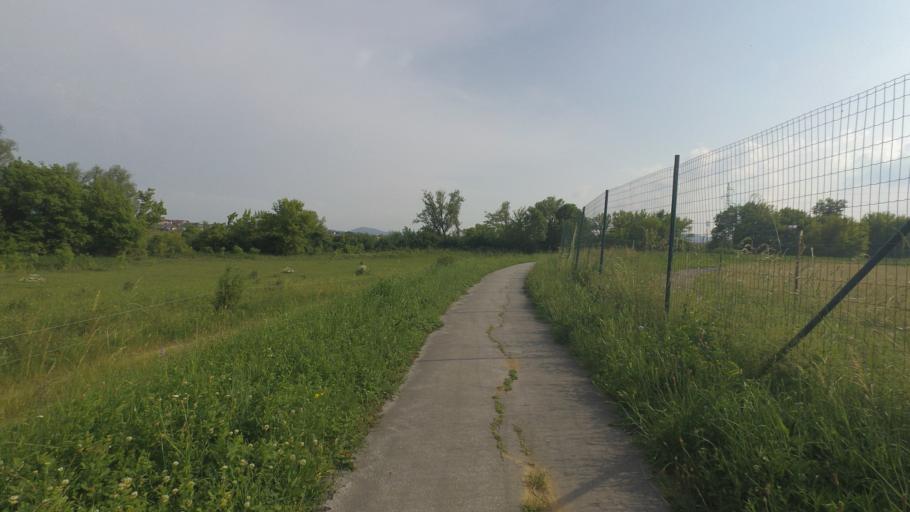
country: HR
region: Karlovacka
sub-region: Grad Karlovac
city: Karlovac
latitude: 45.4907
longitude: 15.5710
